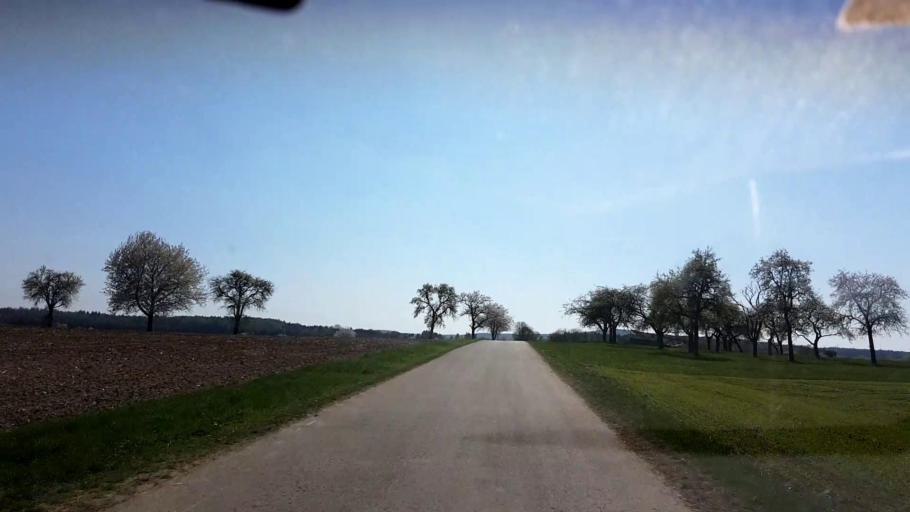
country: DE
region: Bavaria
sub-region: Upper Franconia
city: Heiligenstadt
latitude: 49.8973
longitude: 11.1732
